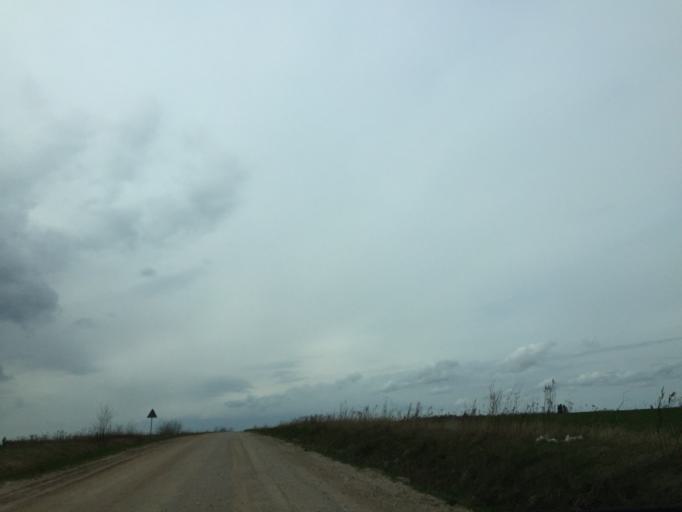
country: LV
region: Priekuli
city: Priekuli
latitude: 57.3419
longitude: 25.3565
